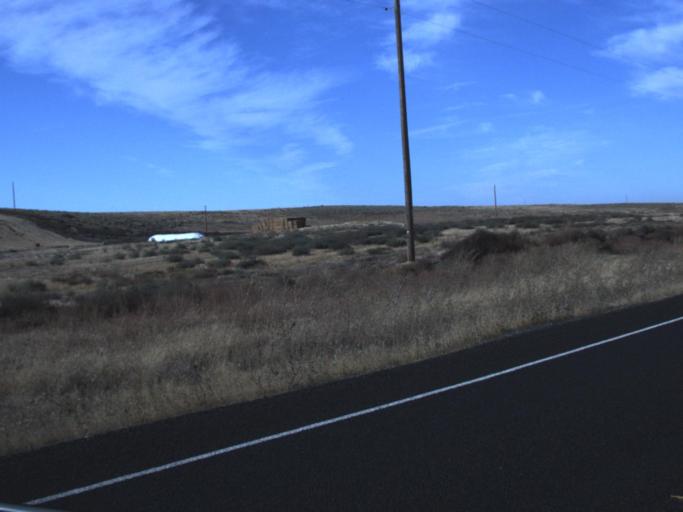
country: US
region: Washington
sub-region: Franklin County
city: Connell
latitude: 46.6347
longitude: -118.8032
